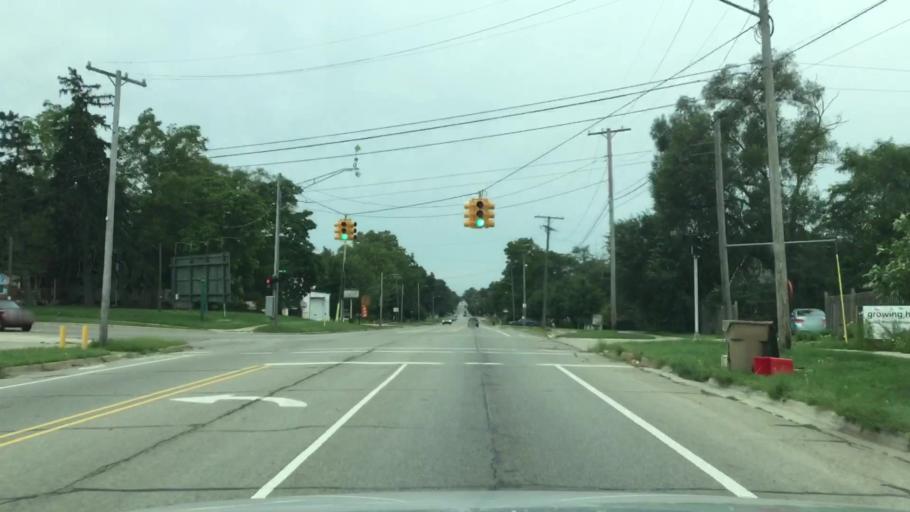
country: US
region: Michigan
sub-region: Washtenaw County
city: Ypsilanti
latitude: 42.2376
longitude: -83.6255
